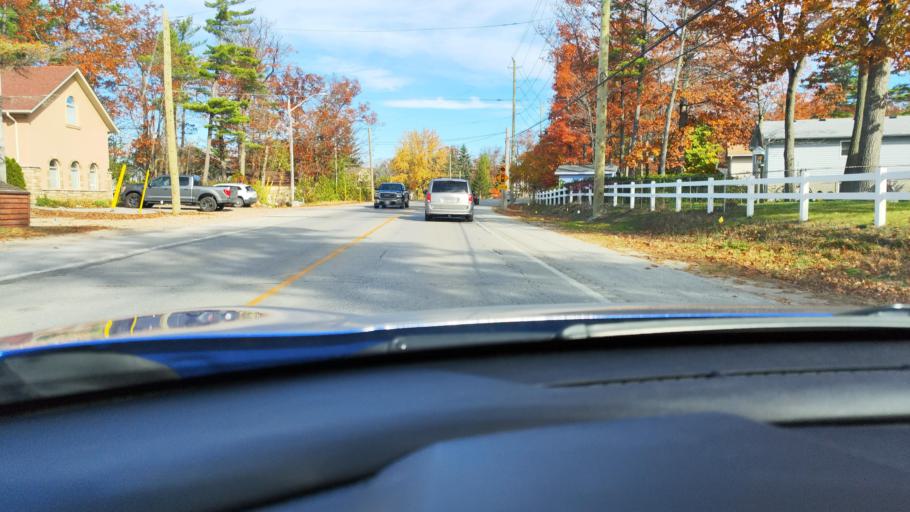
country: CA
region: Ontario
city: Wasaga Beach
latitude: 44.5175
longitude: -80.0199
